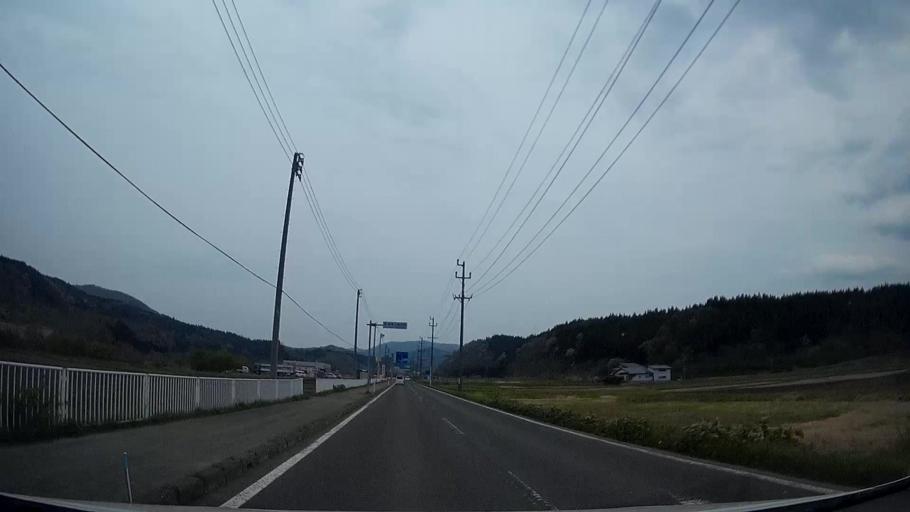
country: JP
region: Akita
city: Hanawa
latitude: 40.2864
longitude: 140.8063
